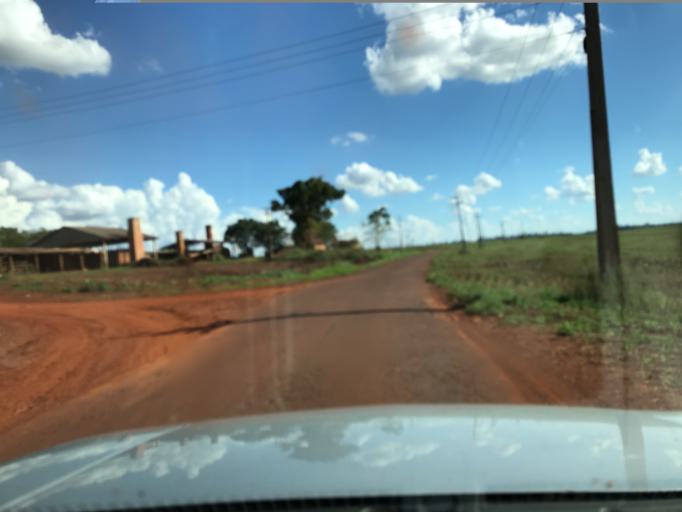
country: BR
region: Parana
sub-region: Palotina
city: Palotina
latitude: -24.2474
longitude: -53.7924
